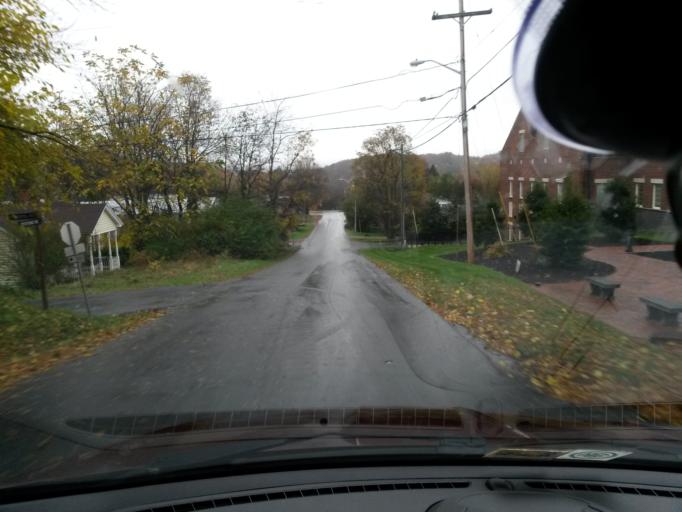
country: US
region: Virginia
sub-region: Botetourt County
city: Fincastle
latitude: 37.5005
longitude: -79.8778
